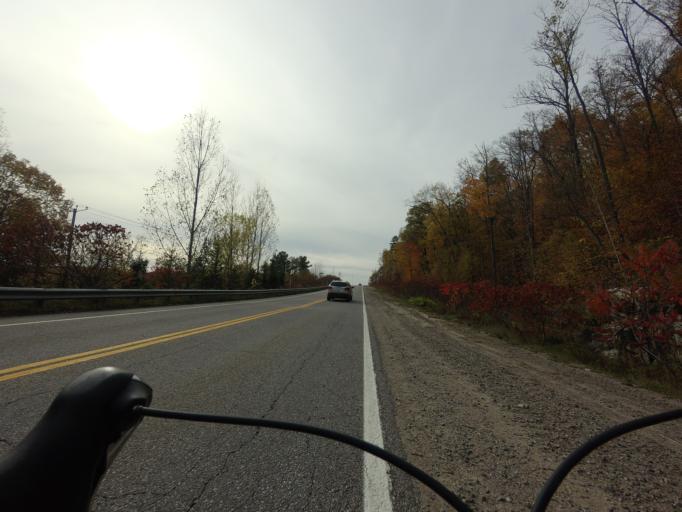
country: CA
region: Quebec
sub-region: Outaouais
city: Val-des-Monts
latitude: 45.6535
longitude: -75.6647
